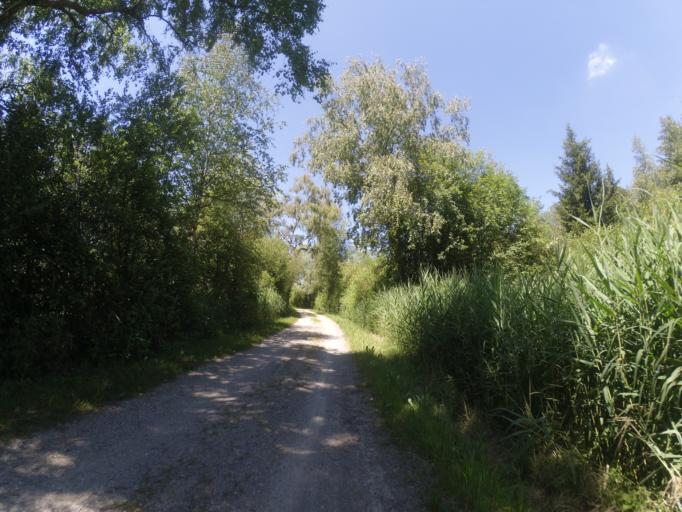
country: DE
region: Baden-Wuerttemberg
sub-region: Tuebingen Region
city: Bad Wurzach
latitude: 47.8981
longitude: 9.8493
